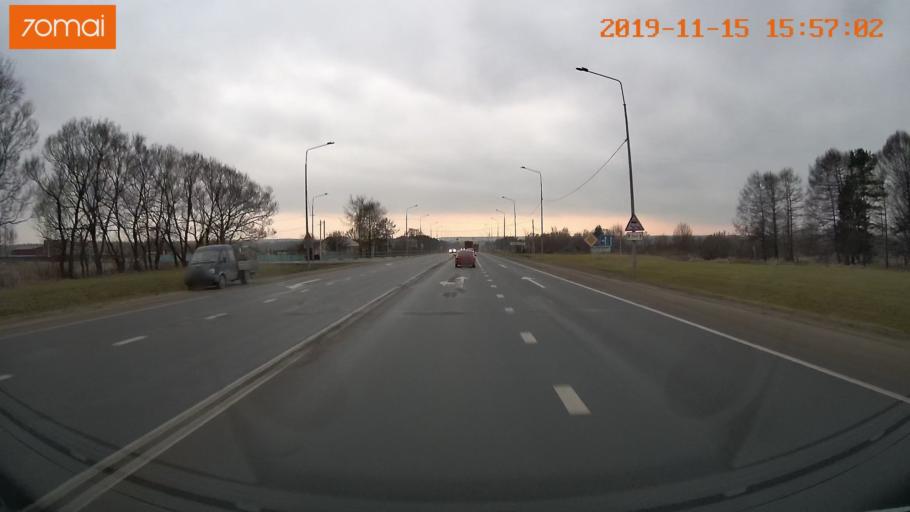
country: RU
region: Jaroslavl
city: Yaroslavl
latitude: 57.8351
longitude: 39.9676
